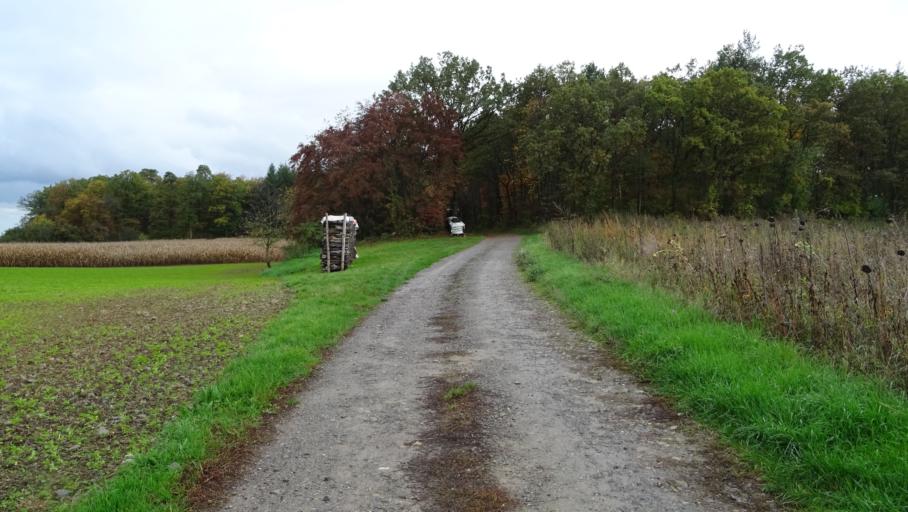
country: DE
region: Baden-Wuerttemberg
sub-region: Karlsruhe Region
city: Billigheim
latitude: 49.3453
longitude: 9.2351
